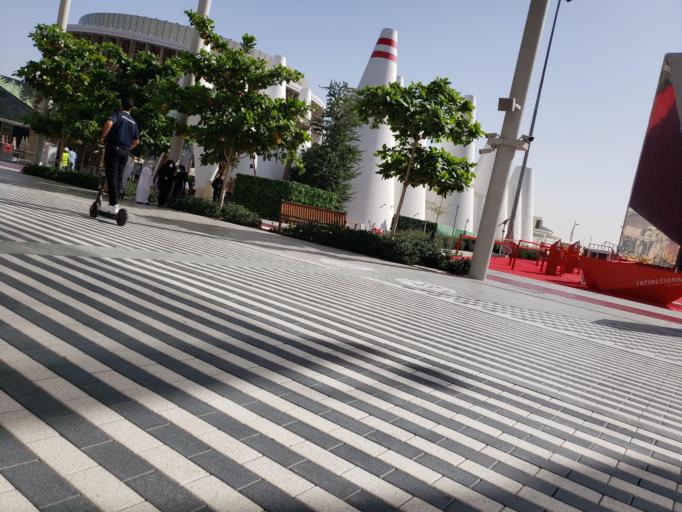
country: AE
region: Dubai
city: Dubai
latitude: 24.9644
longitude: 55.1529
